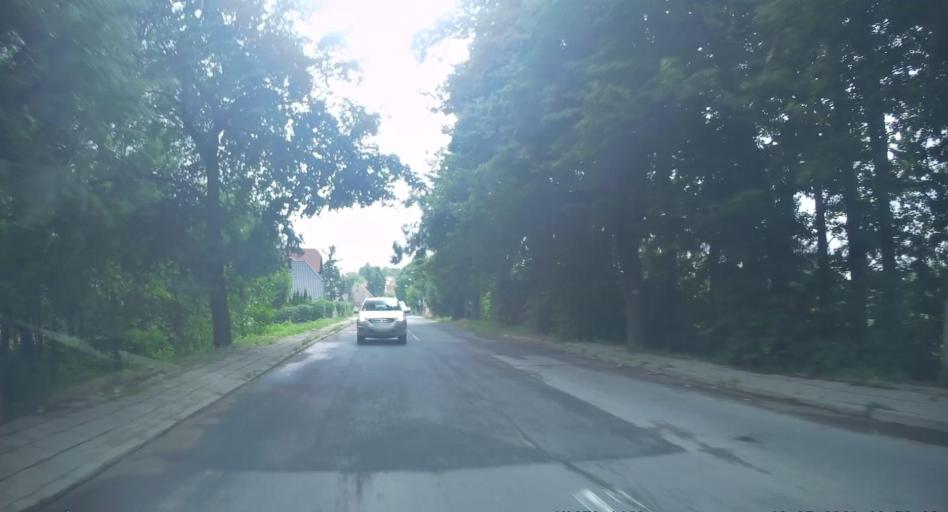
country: PL
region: Opole Voivodeship
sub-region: Powiat nyski
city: Paczkow
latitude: 50.4692
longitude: 17.0136
